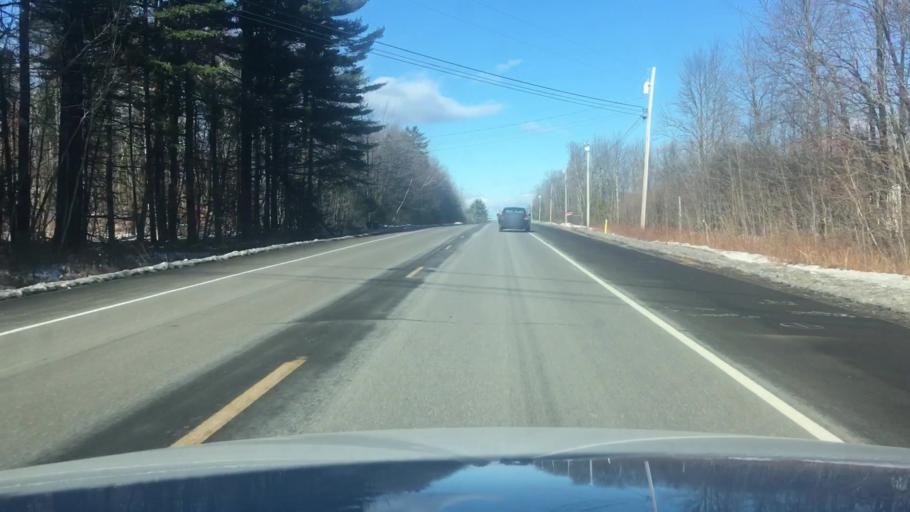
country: US
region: Maine
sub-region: Kennebec County
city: Waterville
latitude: 44.6208
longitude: -69.6718
